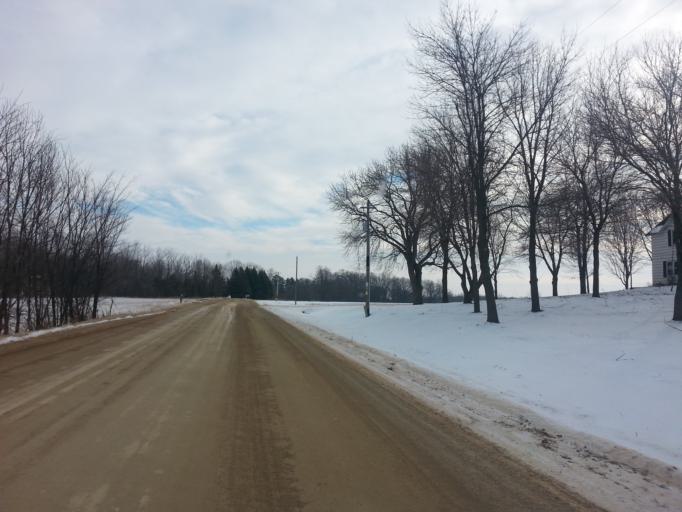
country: US
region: Minnesota
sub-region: Scott County
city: Prior Lake
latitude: 44.7205
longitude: -93.4777
